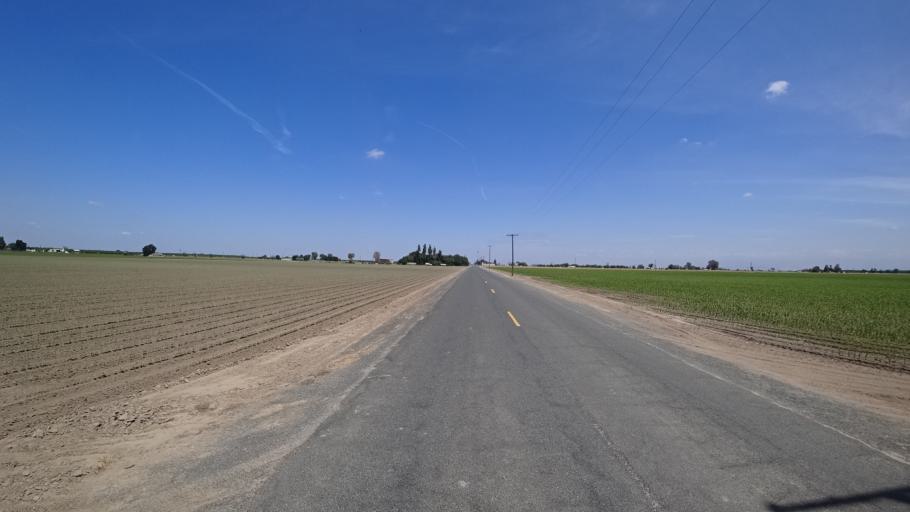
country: US
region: California
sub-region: Tulare County
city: Goshen
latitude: 36.3207
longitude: -119.4754
